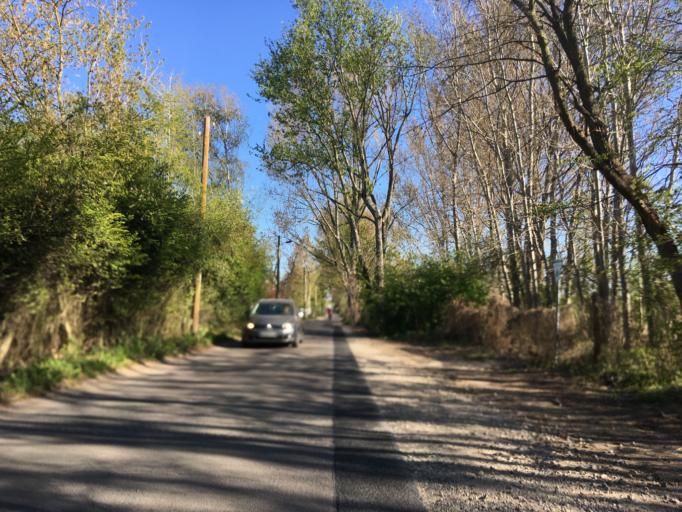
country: DE
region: Berlin
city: Wartenberg
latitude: 52.5827
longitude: 13.4982
